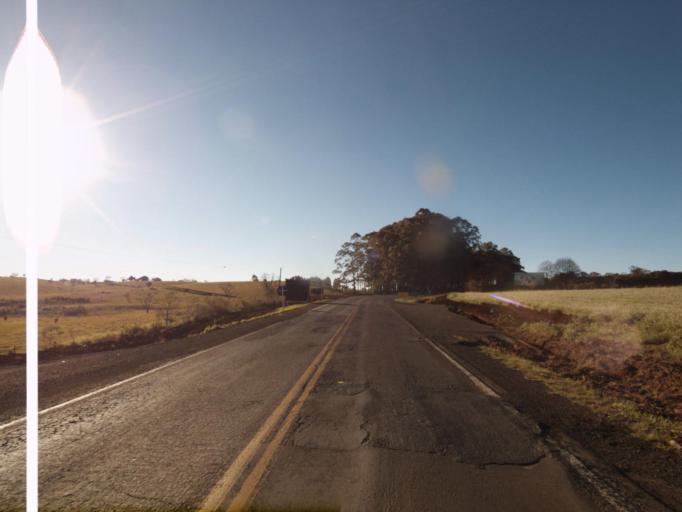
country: AR
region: Misiones
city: Bernardo de Irigoyen
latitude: -26.2899
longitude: -53.5558
